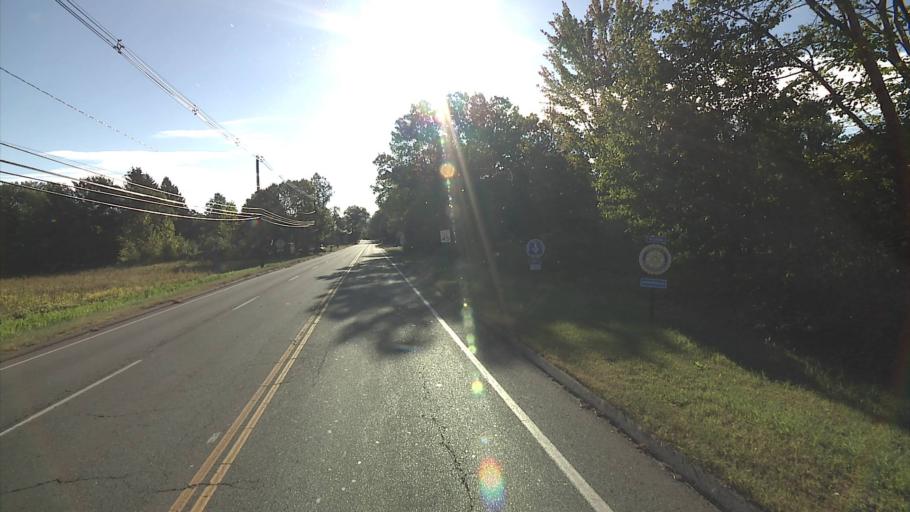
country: US
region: Connecticut
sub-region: New Haven County
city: Wallingford
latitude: 41.4936
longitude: -72.8393
